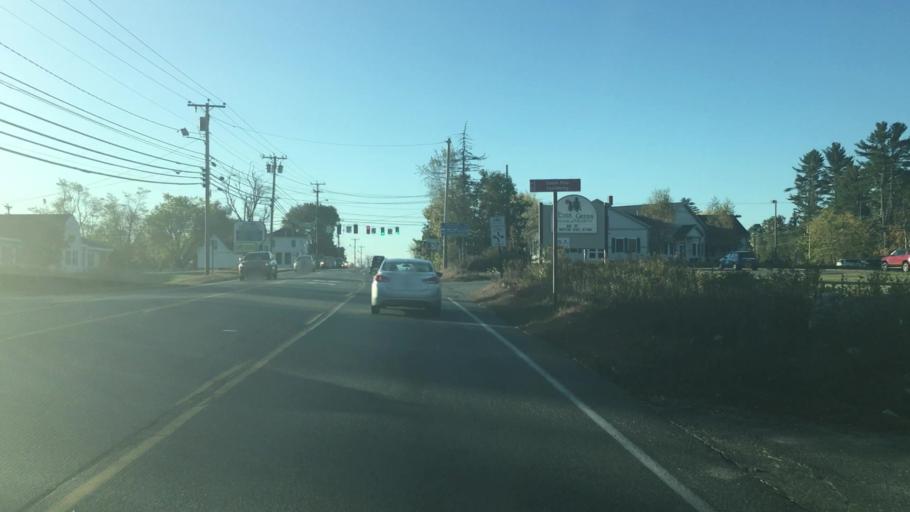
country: US
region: Maine
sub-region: Hancock County
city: Ellsworth
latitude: 44.5205
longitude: -68.3963
